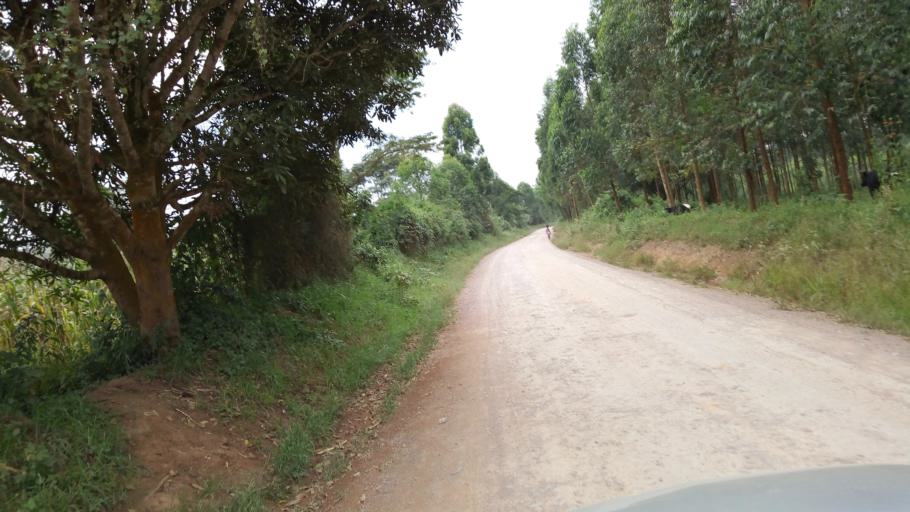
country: UG
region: Central Region
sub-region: Kiboga District
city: Kiboga
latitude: 0.7111
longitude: 31.7575
